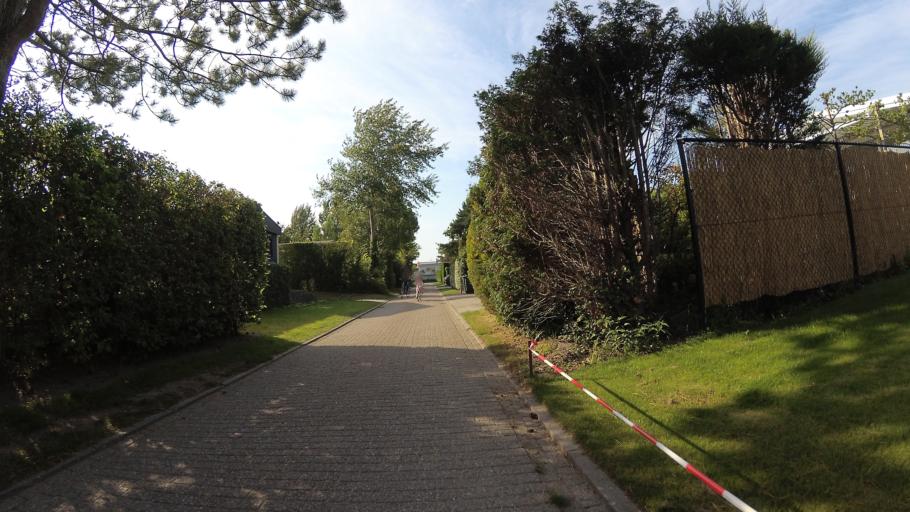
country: NL
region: Zeeland
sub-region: Gemeente Veere
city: Veere
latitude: 51.5635
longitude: 3.6748
